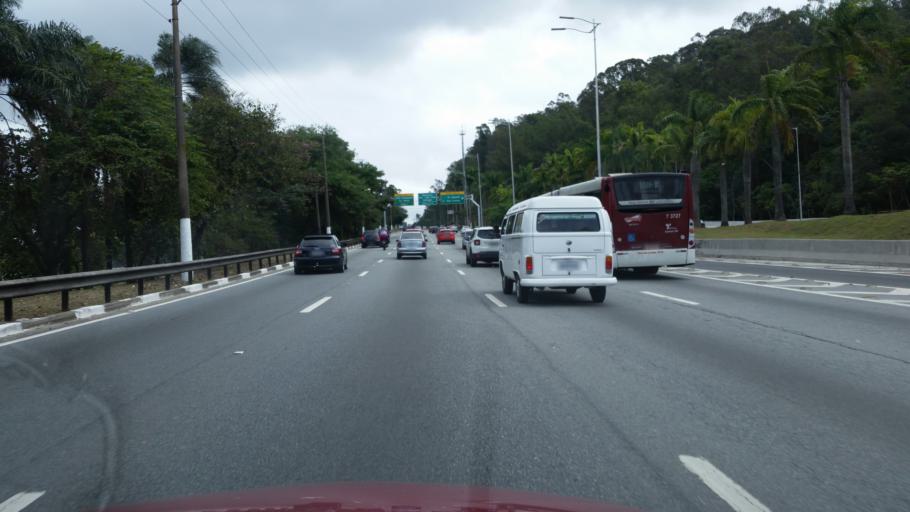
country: BR
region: Sao Paulo
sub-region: Taboao Da Serra
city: Taboao da Serra
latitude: -23.6357
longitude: -46.7220
